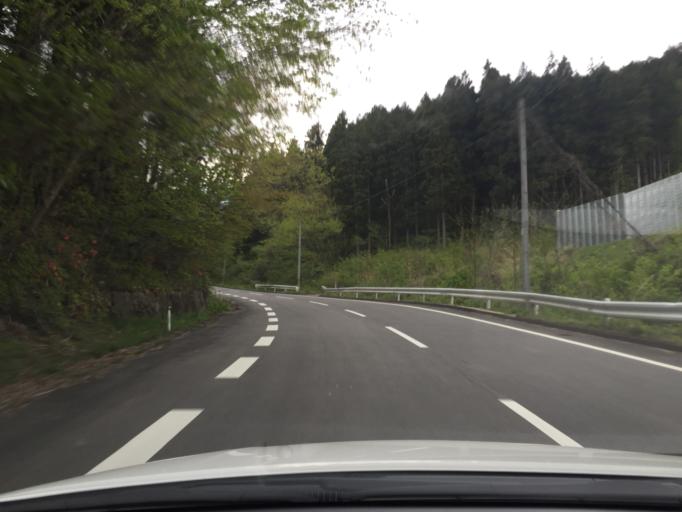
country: JP
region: Fukushima
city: Yanagawamachi-saiwaicho
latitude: 37.7520
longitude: 140.6910
